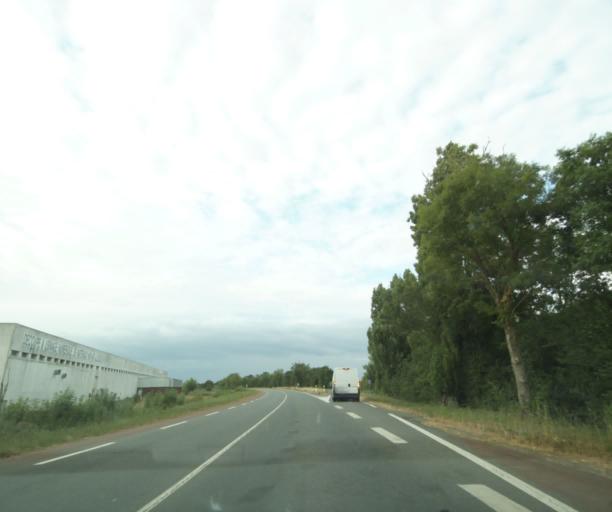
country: FR
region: Poitou-Charentes
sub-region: Departement de la Charente-Maritime
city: Marans
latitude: 46.2834
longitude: -0.9944
